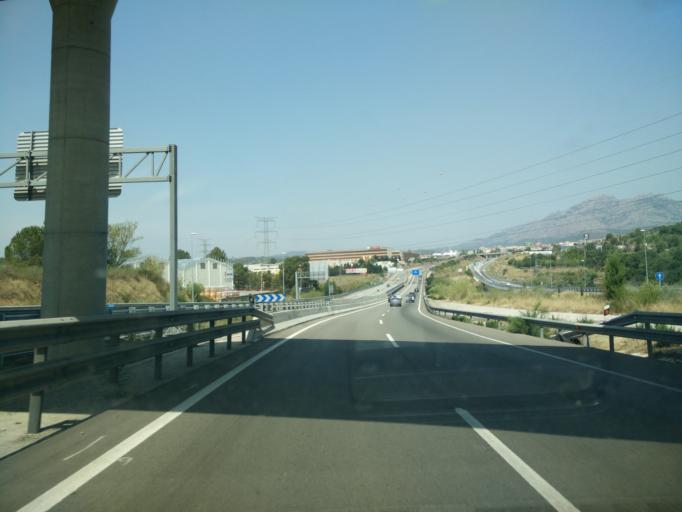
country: ES
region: Catalonia
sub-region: Provincia de Barcelona
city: Abrera
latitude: 41.5228
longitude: 1.8866
